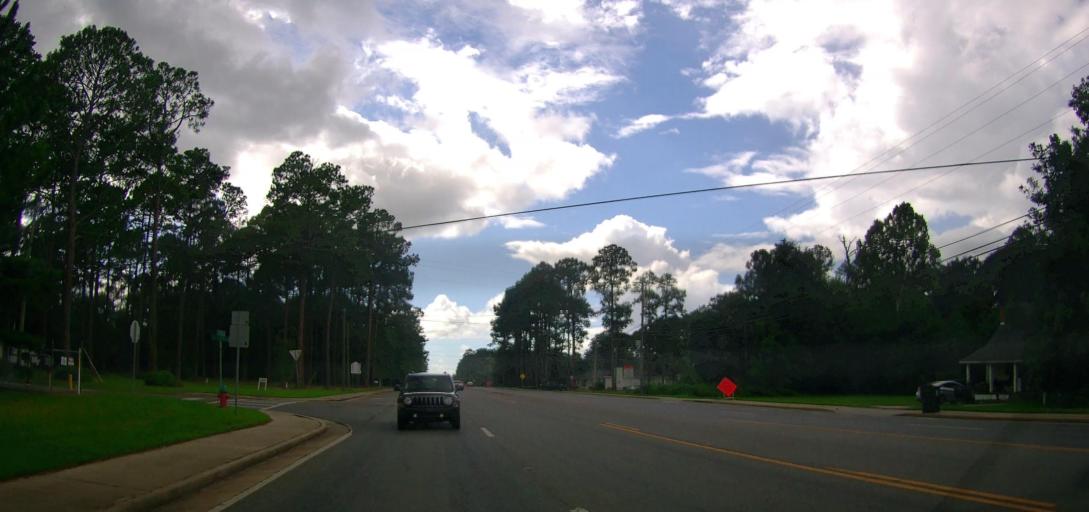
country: US
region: Georgia
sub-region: Coffee County
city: Douglas
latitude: 31.5136
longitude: -82.8738
